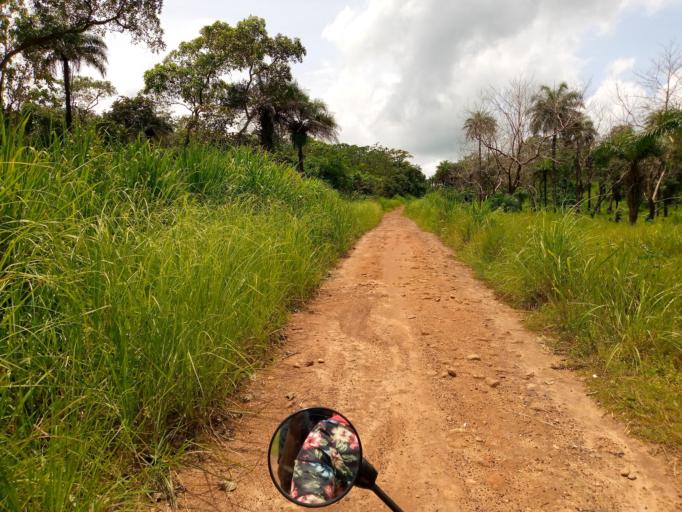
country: SL
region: Northern Province
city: Binkolo
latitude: 9.1205
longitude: -12.1336
